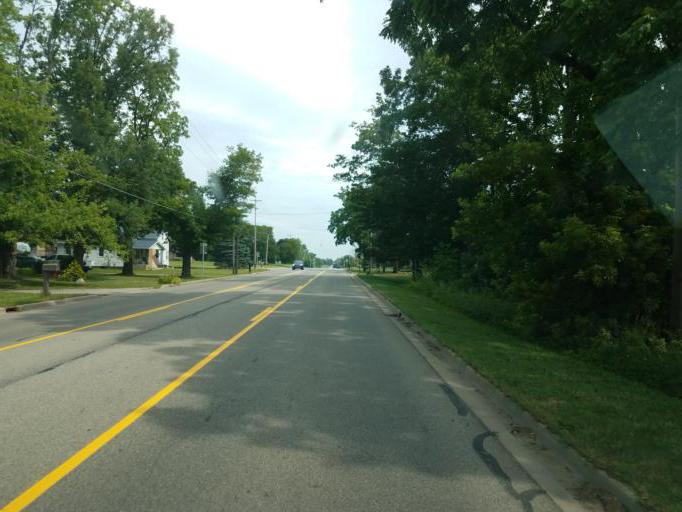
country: US
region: Michigan
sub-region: Eaton County
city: Charlotte
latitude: 42.5779
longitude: -84.8359
